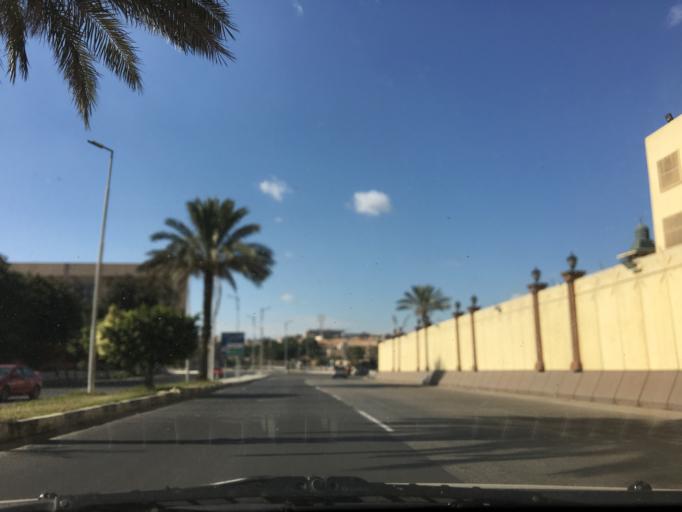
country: EG
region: Muhafazat al Qahirah
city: Cairo
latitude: 30.0506
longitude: 31.3091
